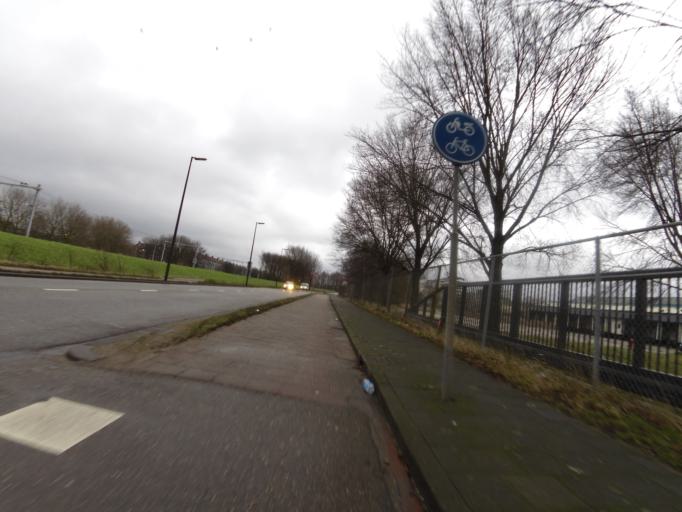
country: NL
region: South Holland
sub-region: Gemeente Vlaardingen
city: Vlaardingen
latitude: 51.9011
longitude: 4.3351
